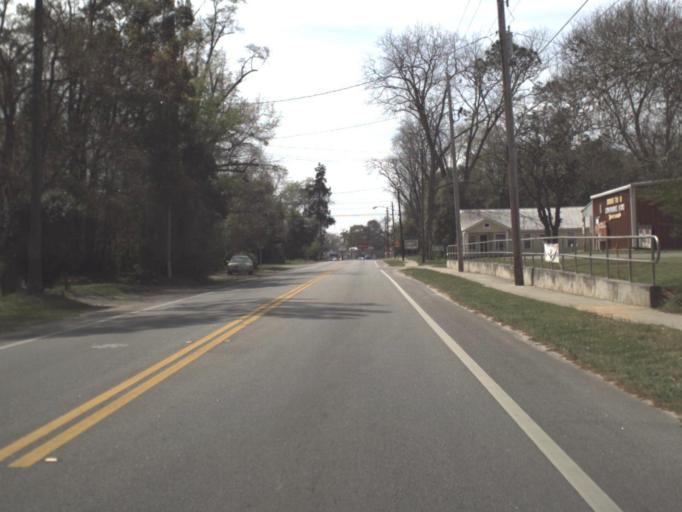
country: US
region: Florida
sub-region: Jackson County
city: Graceville
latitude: 30.9655
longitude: -85.5141
